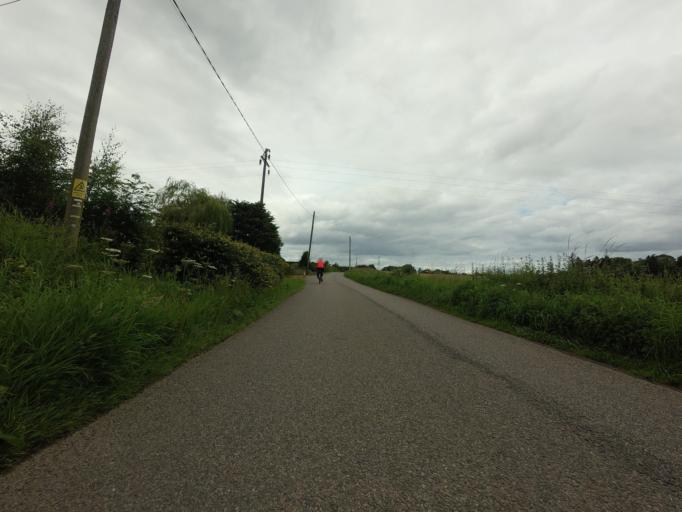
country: GB
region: Scotland
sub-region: Moray
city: Forres
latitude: 57.5970
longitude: -3.7167
